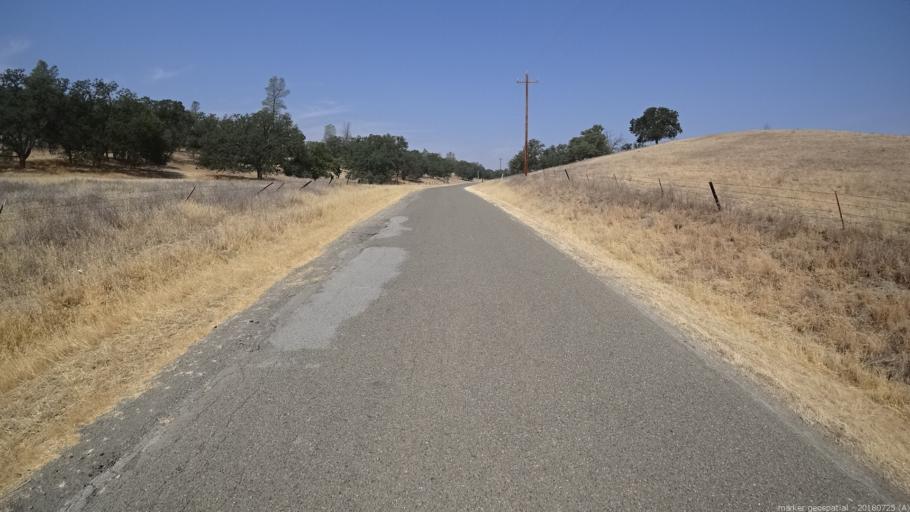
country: US
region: California
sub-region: San Luis Obispo County
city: Shandon
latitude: 35.8633
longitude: -120.3984
